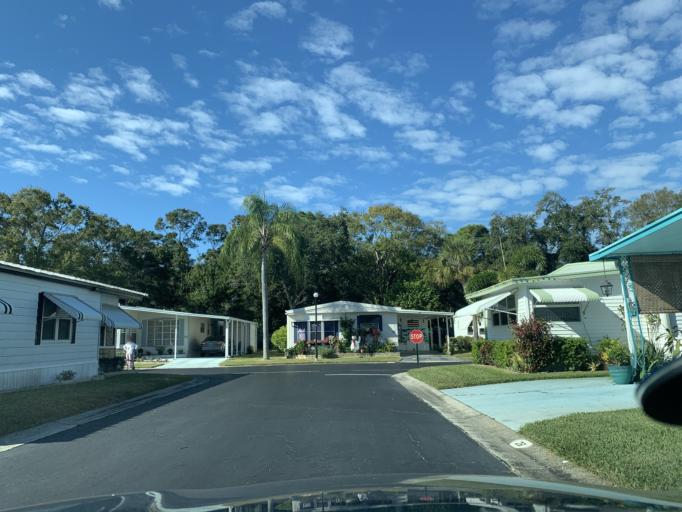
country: US
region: Florida
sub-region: Pinellas County
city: Kenneth City
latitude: 27.8162
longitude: -82.7470
